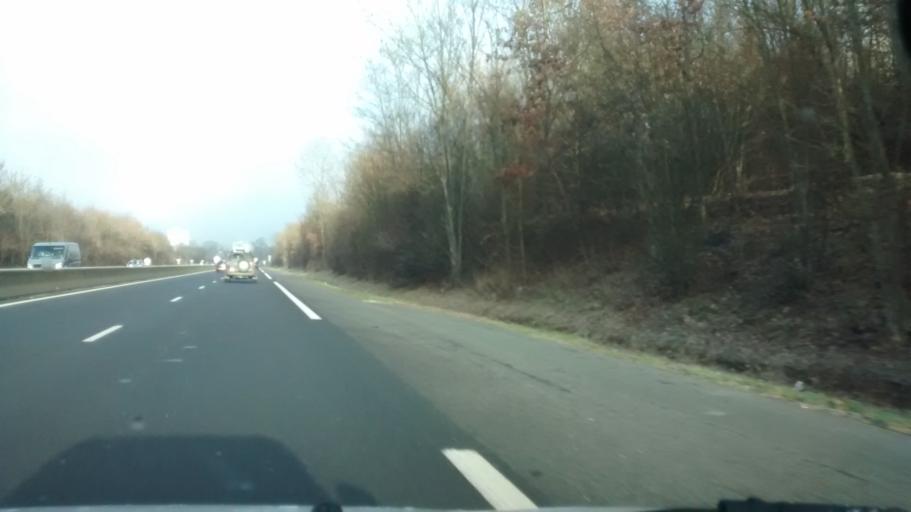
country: FR
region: Centre
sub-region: Departement d'Indre-et-Loire
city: Joue-les-Tours
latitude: 47.3345
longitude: 0.6717
